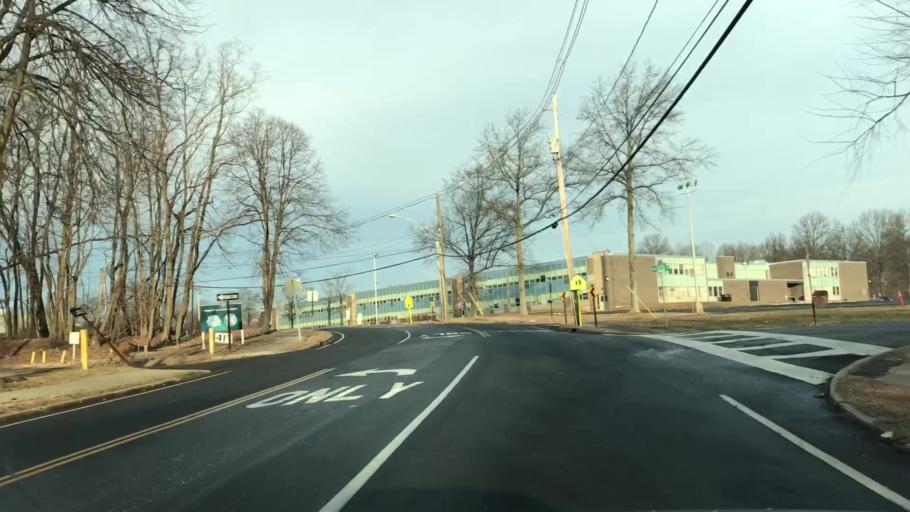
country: US
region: New York
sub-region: Rockland County
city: Kaser
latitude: 41.1345
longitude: -74.0607
